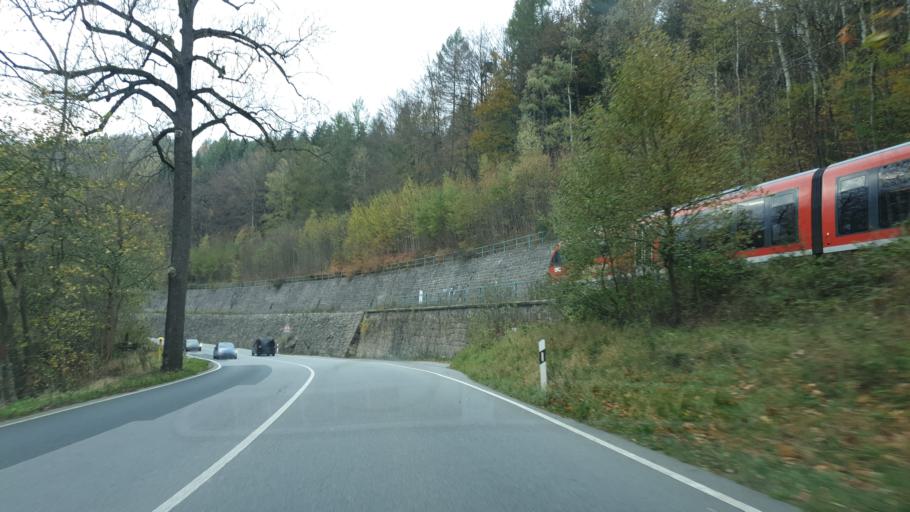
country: DE
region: Saxony
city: Breitenbrunn
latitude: 50.5057
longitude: 12.7684
